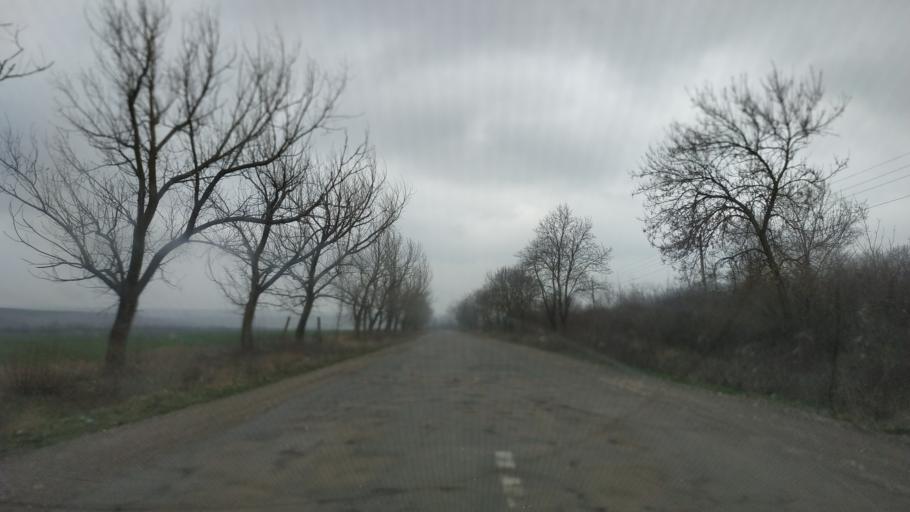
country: MD
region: Gagauzia
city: Bugeac
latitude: 46.3475
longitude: 28.7800
